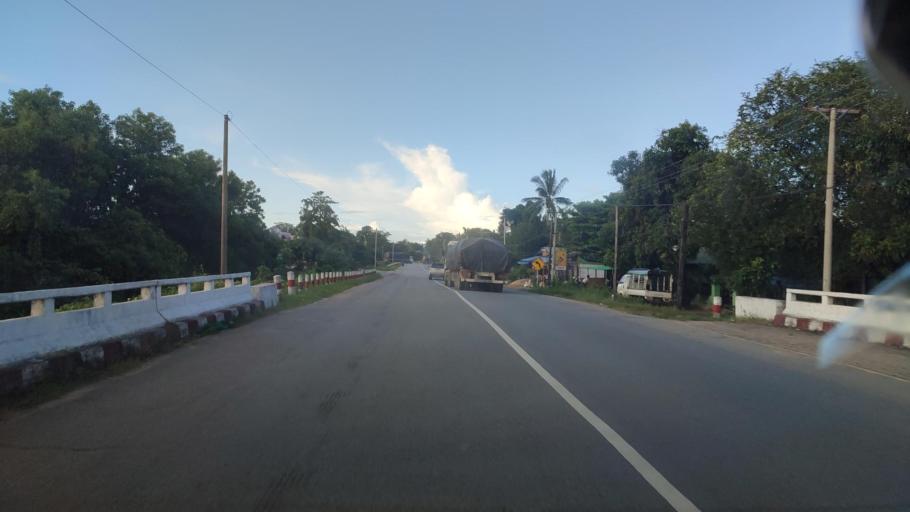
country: MM
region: Bago
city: Bago
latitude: 17.5773
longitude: 96.5553
